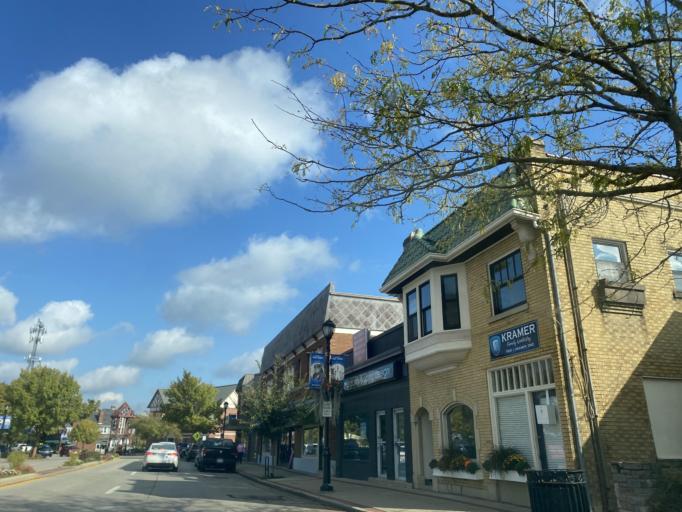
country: US
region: Kentucky
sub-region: Campbell County
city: Fort Thomas
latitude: 39.0790
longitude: -84.4485
